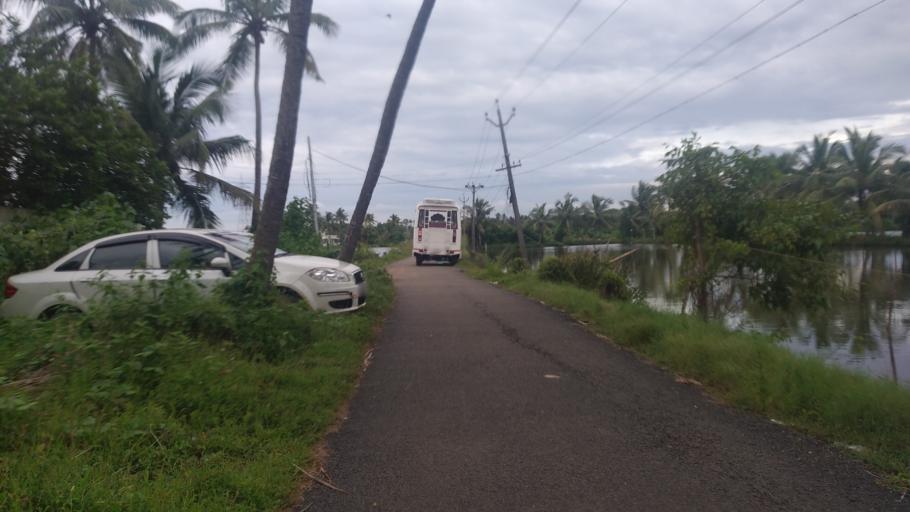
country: IN
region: Kerala
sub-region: Alappuzha
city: Arukutti
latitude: 9.8699
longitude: 76.2800
